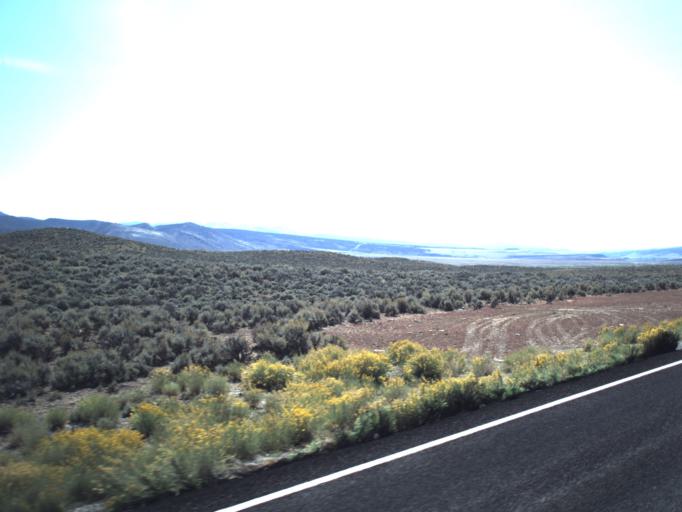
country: US
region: Utah
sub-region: Piute County
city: Junction
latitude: 38.2232
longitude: -111.9986
